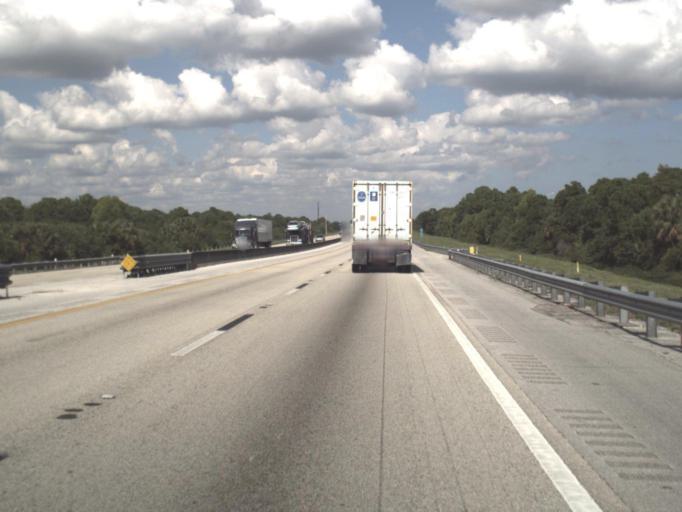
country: US
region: Florida
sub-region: Palm Beach County
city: Limestone Creek
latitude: 26.8994
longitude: -80.1382
